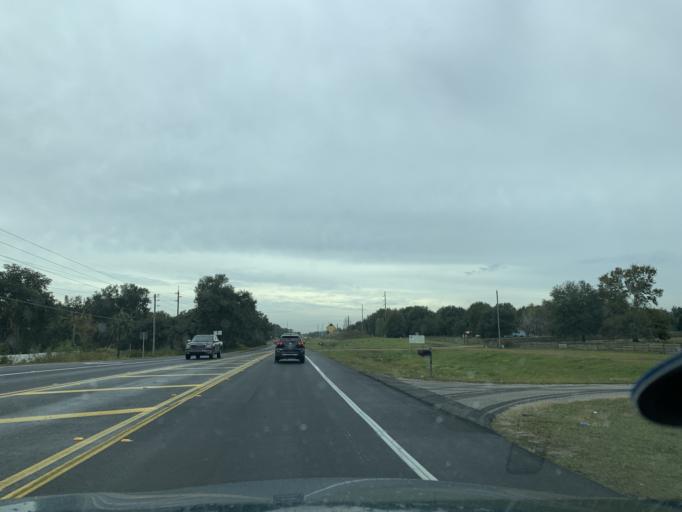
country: US
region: Florida
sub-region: Pasco County
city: Zephyrhills West
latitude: 28.2271
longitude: -82.2464
